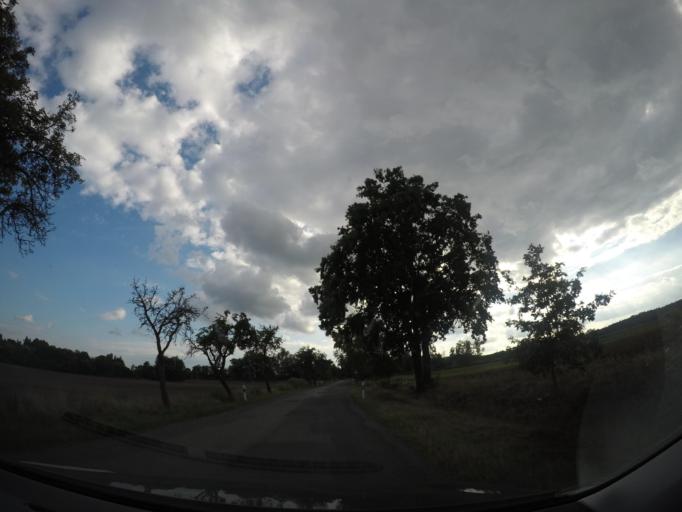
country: DE
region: Saxony-Anhalt
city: Mieste
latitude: 52.4712
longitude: 11.1344
